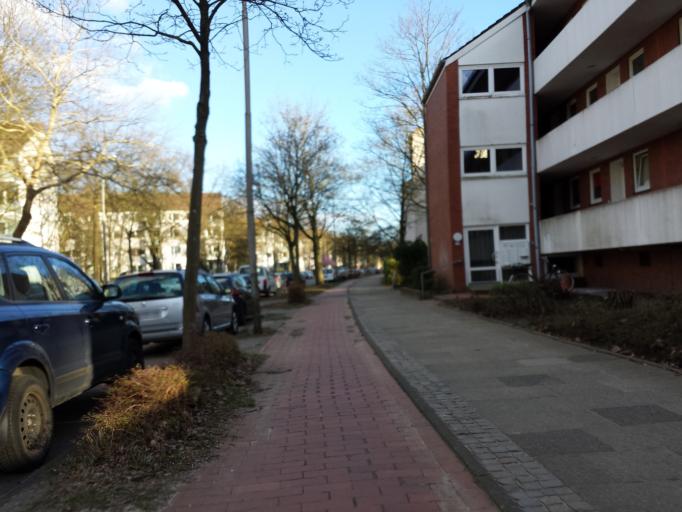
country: DE
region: Bremen
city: Bremen
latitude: 53.0969
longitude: 8.8460
